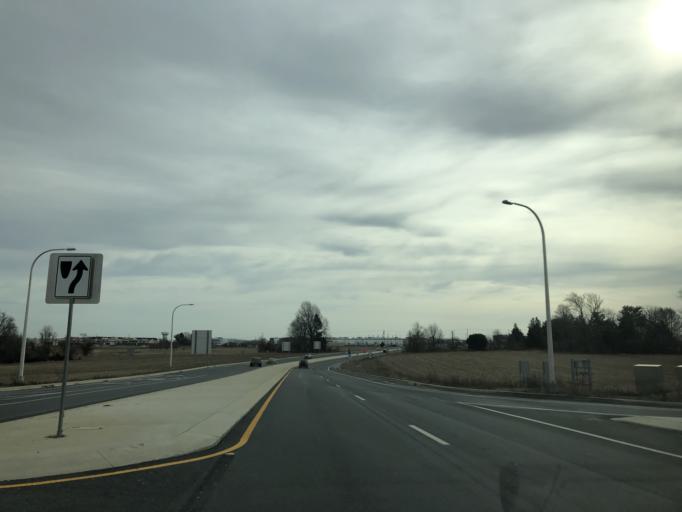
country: US
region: Delaware
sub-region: New Castle County
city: Middletown
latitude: 39.4443
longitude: -75.7507
